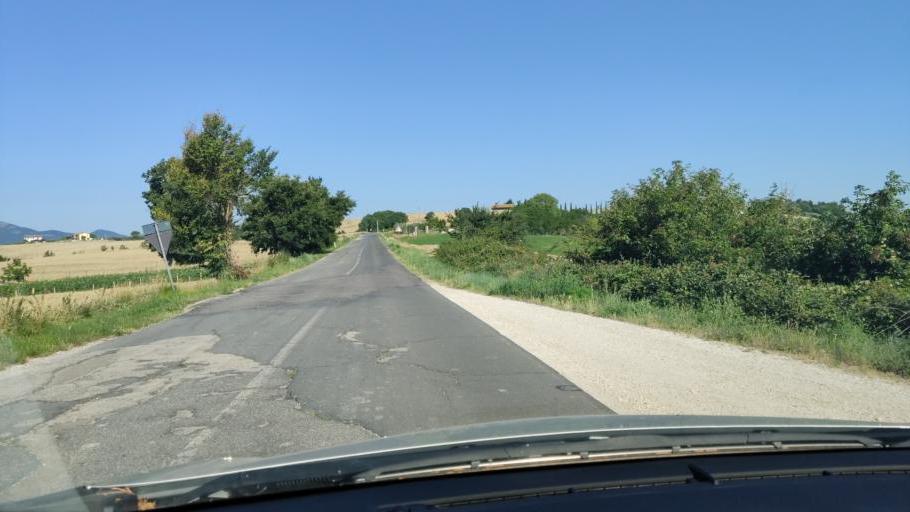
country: IT
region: Umbria
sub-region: Provincia di Terni
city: Avigliano Umbro
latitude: 42.6721
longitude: 12.4435
